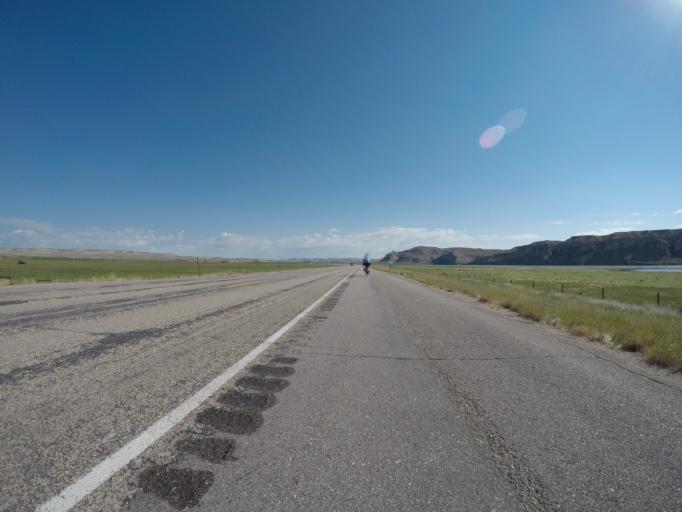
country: US
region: Wyoming
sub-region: Sublette County
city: Marbleton
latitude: 42.1366
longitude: -110.1869
